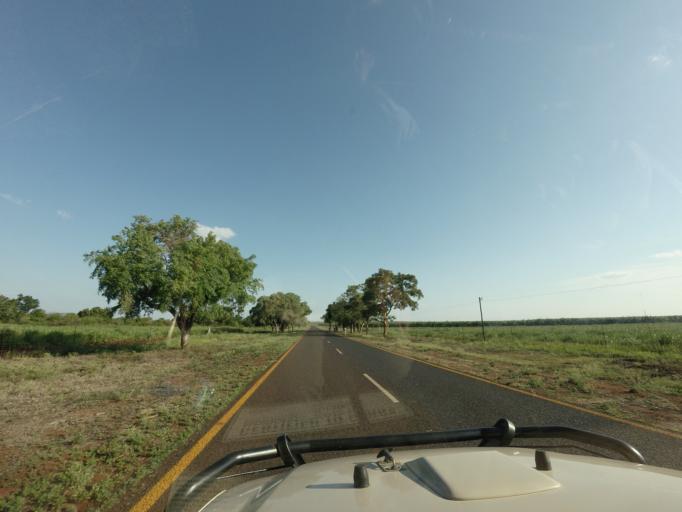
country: ZA
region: Mpumalanga
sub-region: Ehlanzeni District
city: Komatipoort
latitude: -25.3839
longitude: 31.9106
